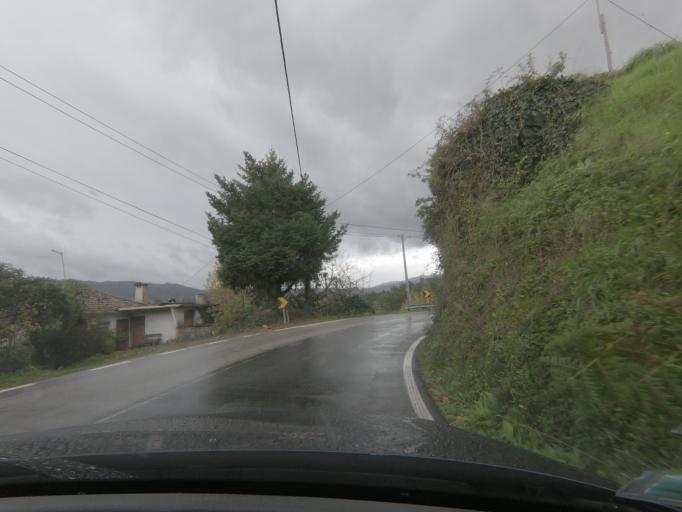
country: PT
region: Vila Real
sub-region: Mondim de Basto
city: Mondim de Basto
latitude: 41.4144
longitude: -7.9768
